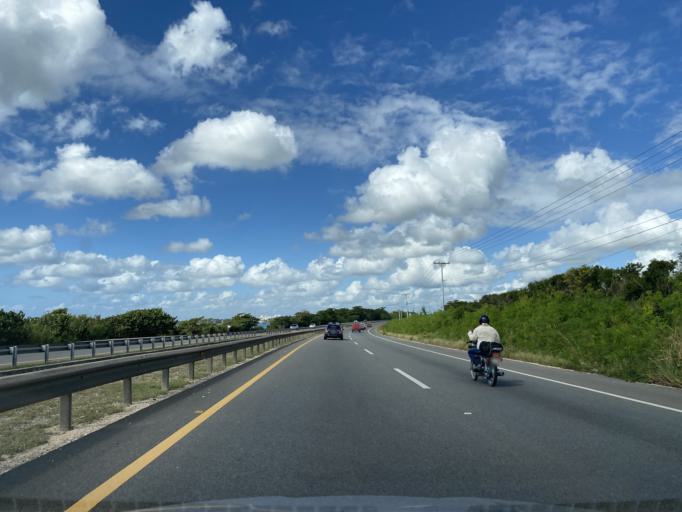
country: DO
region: Santo Domingo
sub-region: Santo Domingo
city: Boca Chica
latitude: 18.4437
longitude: -69.5852
